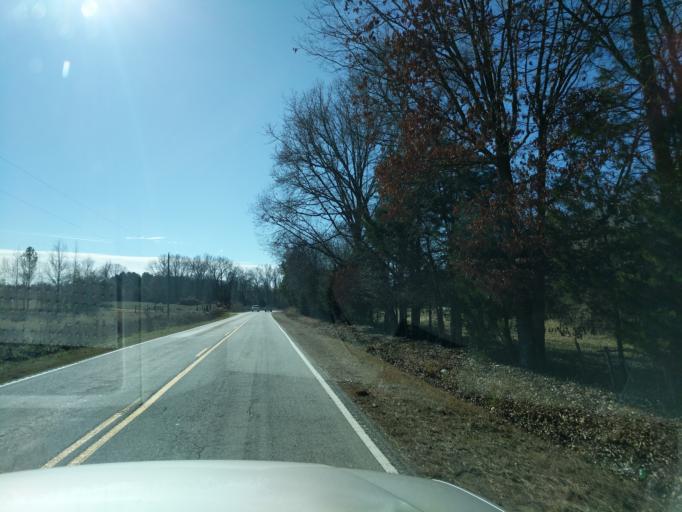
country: US
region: South Carolina
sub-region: Laurens County
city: Joanna
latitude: 34.2929
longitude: -81.8447
